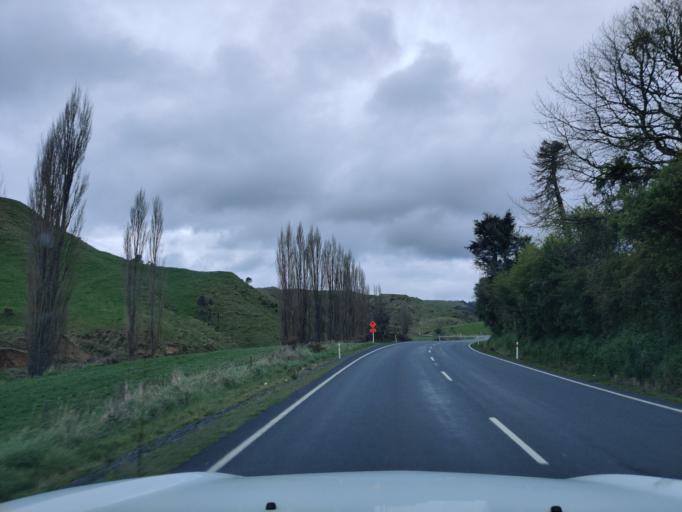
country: NZ
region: Waikato
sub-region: Otorohanga District
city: Otorohanga
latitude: -38.5193
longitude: 175.1916
